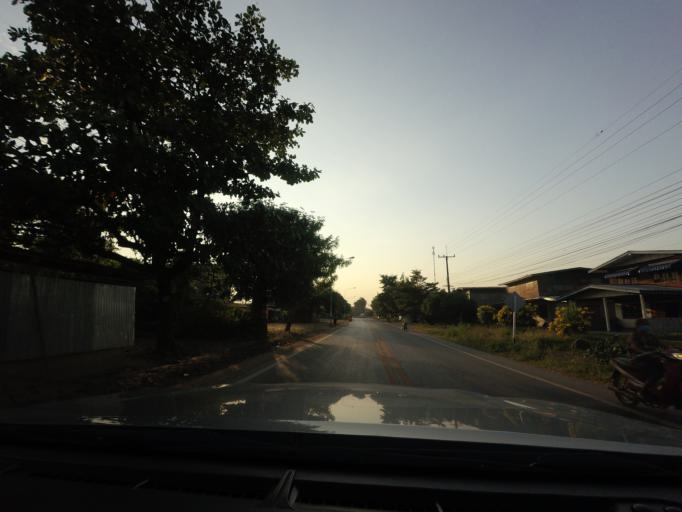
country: TH
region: Phitsanulok
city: Noen Maprang
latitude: 16.6897
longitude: 100.5418
